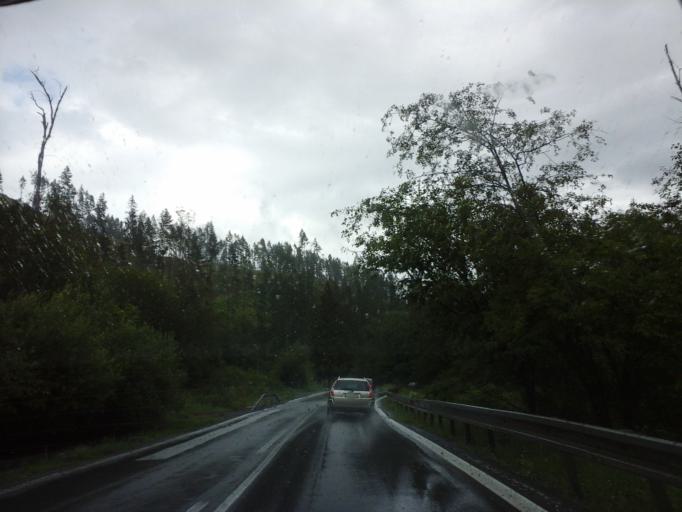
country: SK
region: Presovsky
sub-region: Okres Poprad
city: Poprad
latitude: 48.9620
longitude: 20.2921
